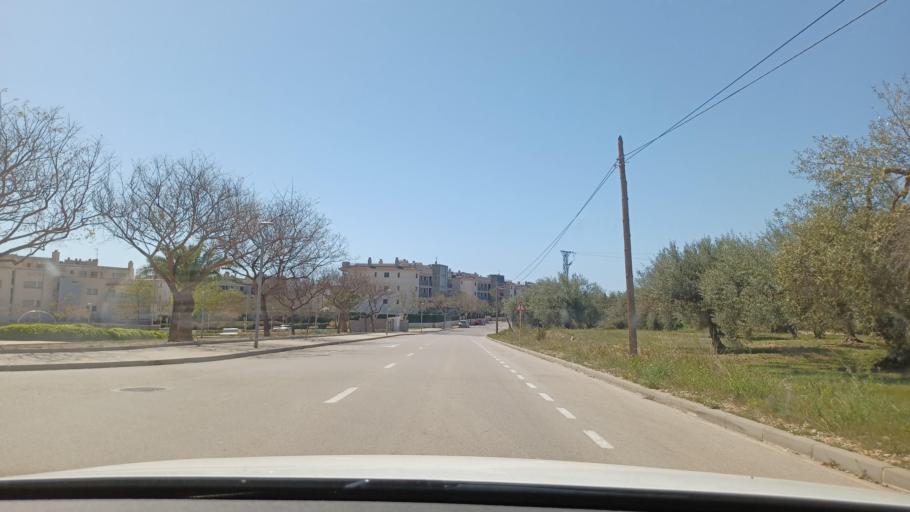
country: ES
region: Catalonia
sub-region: Provincia de Tarragona
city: Sant Carles de la Rapita
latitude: 40.6128
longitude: 0.5831
